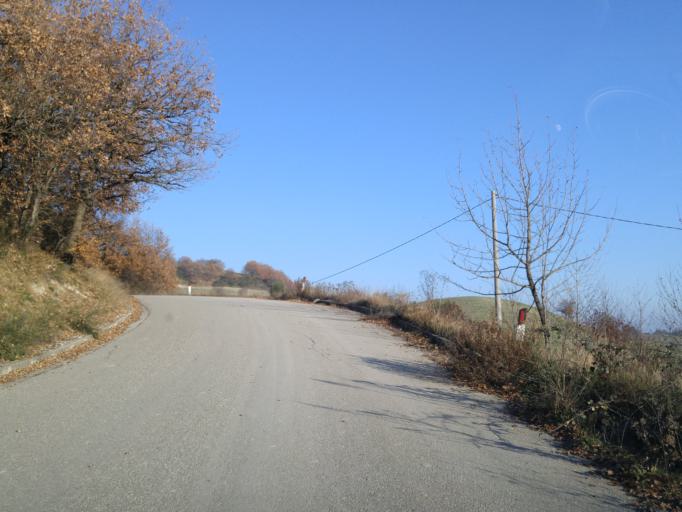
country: IT
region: The Marches
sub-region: Provincia di Pesaro e Urbino
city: Mombaroccio
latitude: 43.7734
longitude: 12.8278
